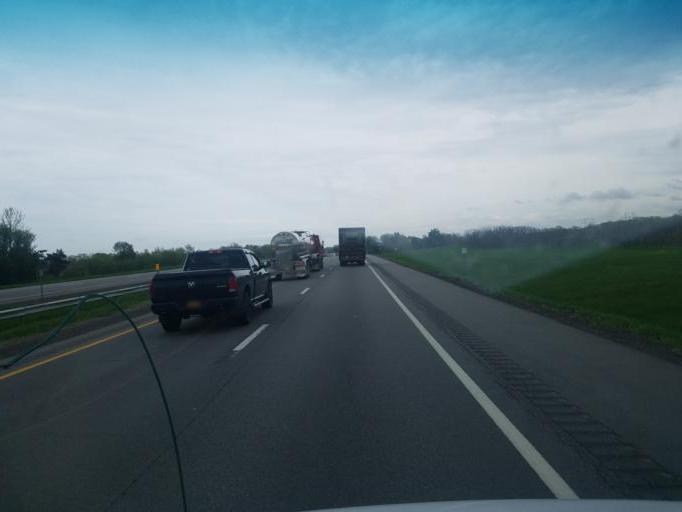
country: US
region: New York
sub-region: Chautauqua County
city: Silver Creek
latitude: 42.5123
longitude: -79.1790
